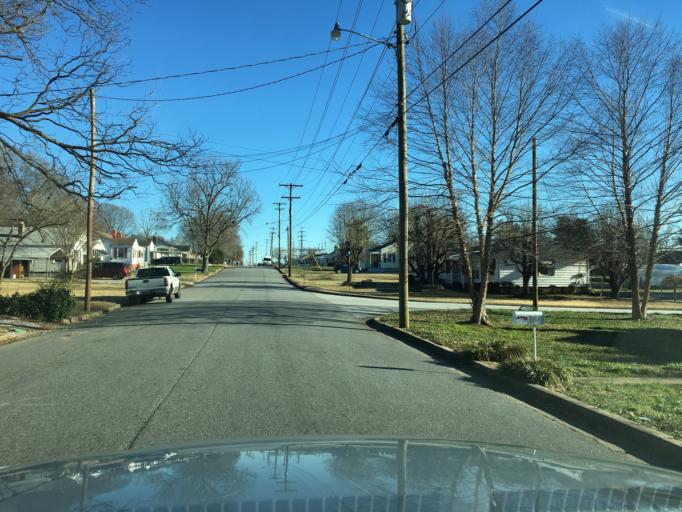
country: US
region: South Carolina
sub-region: Greenville County
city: Greer
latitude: 34.9397
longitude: -82.2377
